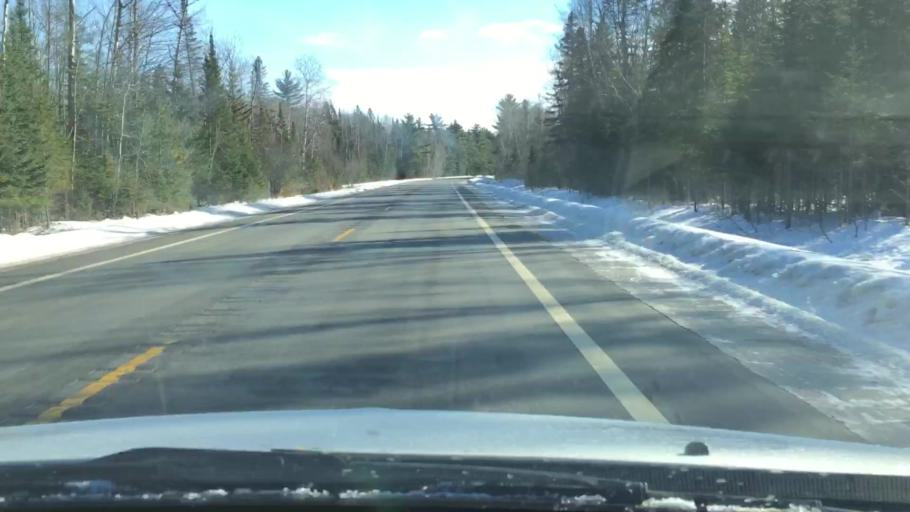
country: US
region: Michigan
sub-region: Charlevoix County
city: East Jordan
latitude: 45.0567
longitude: -85.0744
